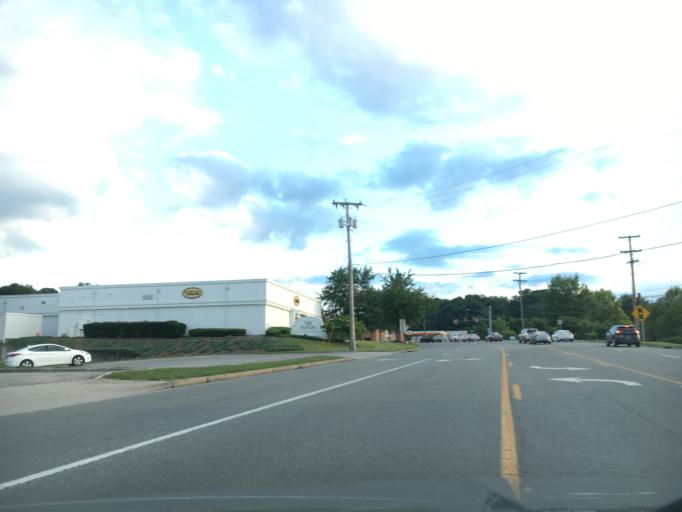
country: US
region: Virginia
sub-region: Roanoke County
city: Cave Spring
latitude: 37.2230
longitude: -79.9849
